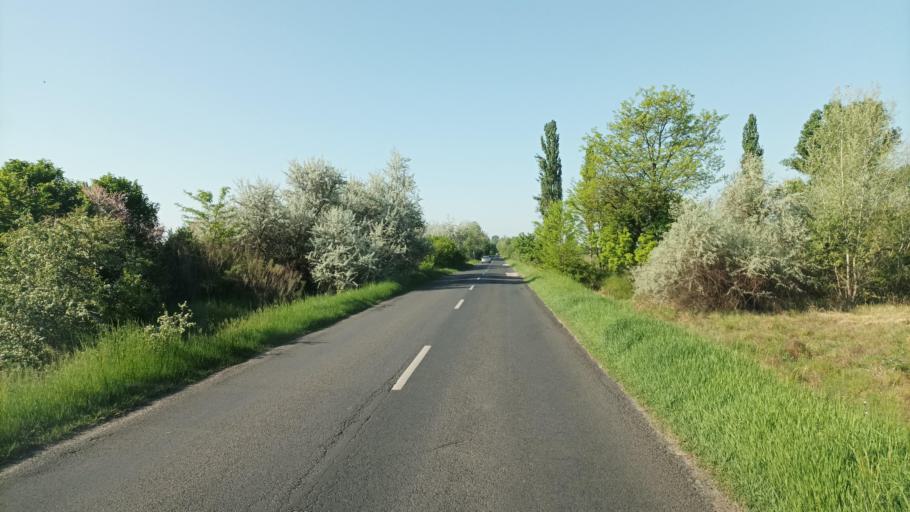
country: HU
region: Pest
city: Monor
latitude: 47.3124
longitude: 19.4436
